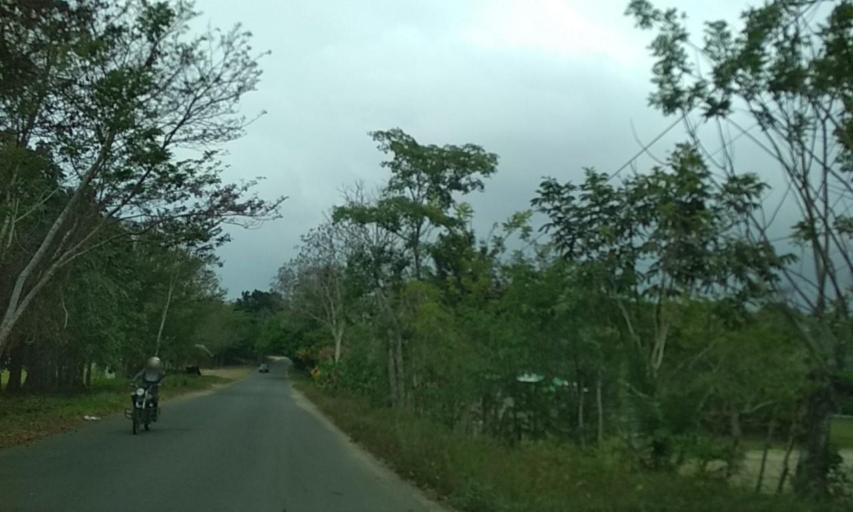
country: MX
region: Tabasco
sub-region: Huimanguillo
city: Francisco Rueda
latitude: 17.6093
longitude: -94.0924
